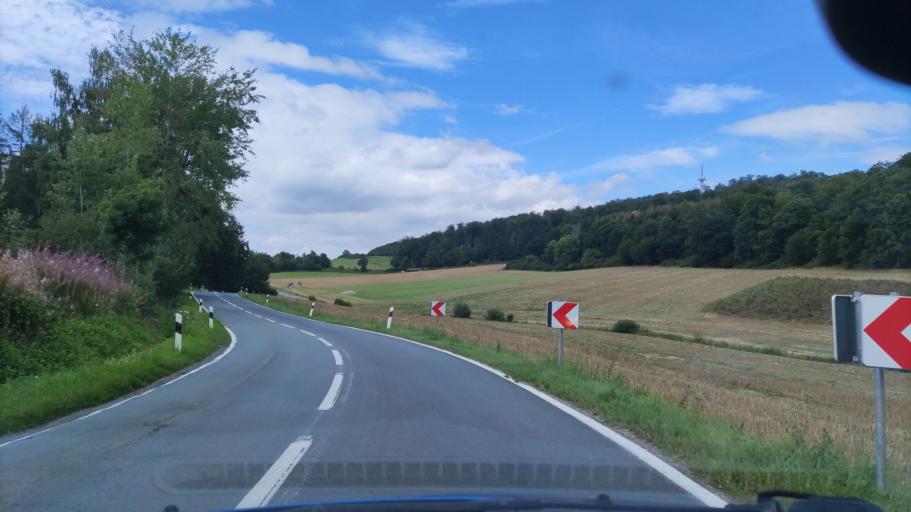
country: DE
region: Lower Saxony
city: Delligsen
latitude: 51.9557
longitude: 9.7880
